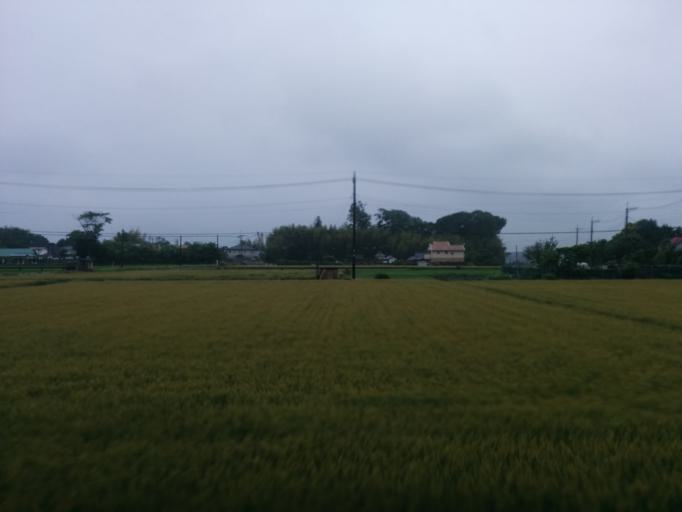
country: JP
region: Tochigi
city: Utsunomiya-shi
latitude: 36.5384
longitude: 139.8411
